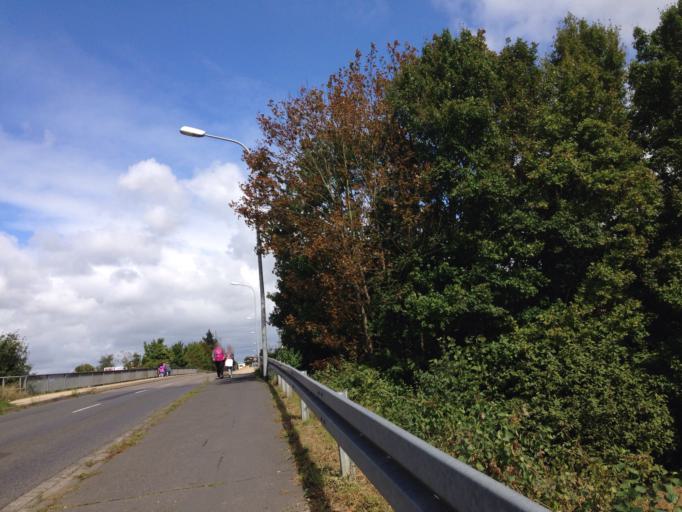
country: DE
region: Hesse
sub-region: Regierungsbezirk Giessen
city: Limburg an der Lahn
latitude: 50.4018
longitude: 8.0627
